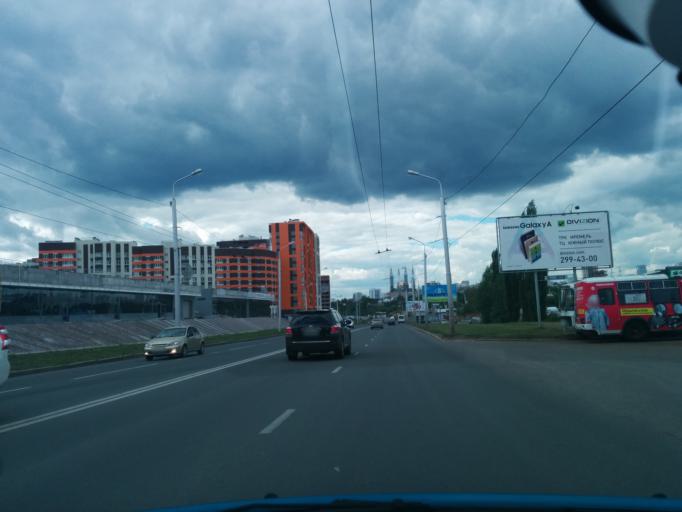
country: RU
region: Bashkortostan
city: Ufa
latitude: 54.7191
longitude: 55.9845
